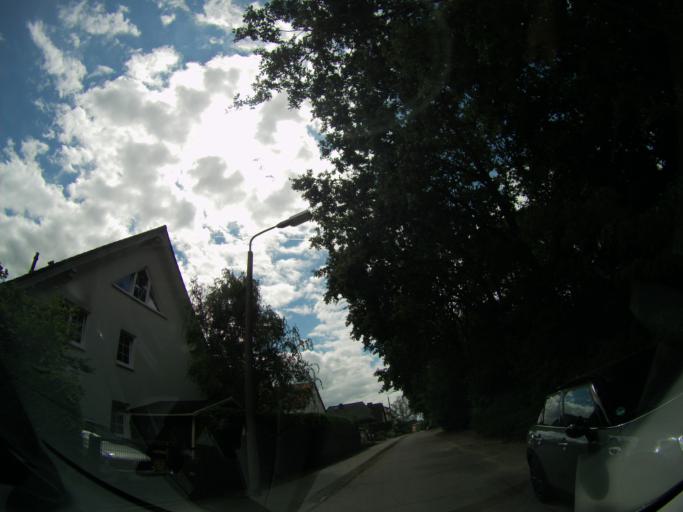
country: DE
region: Brandenburg
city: Teltow
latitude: 52.3957
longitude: 13.2857
